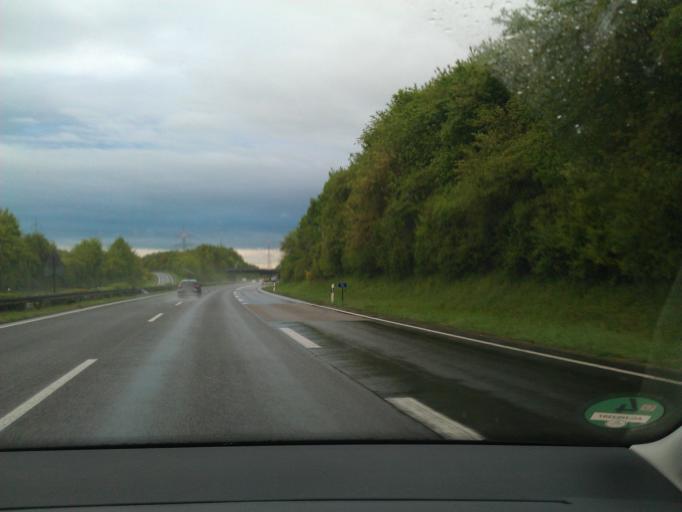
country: DE
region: North Rhine-Westphalia
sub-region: Regierungsbezirk Koln
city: Stossdorf
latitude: 50.7758
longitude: 7.2489
